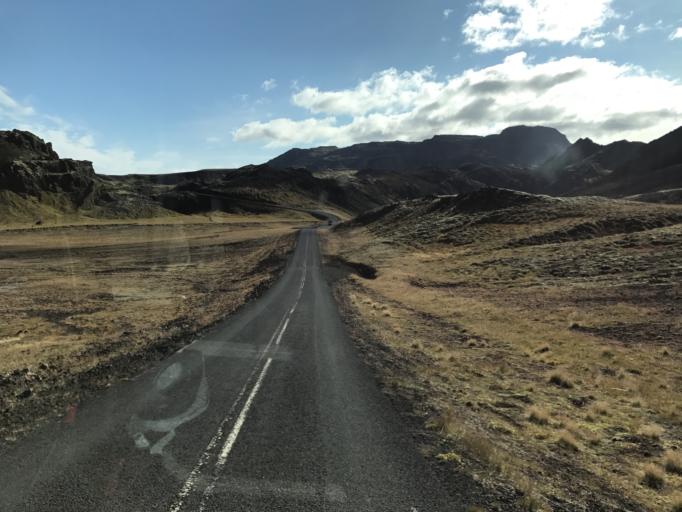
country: IS
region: South
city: Hveragerdi
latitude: 64.1201
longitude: -21.3026
